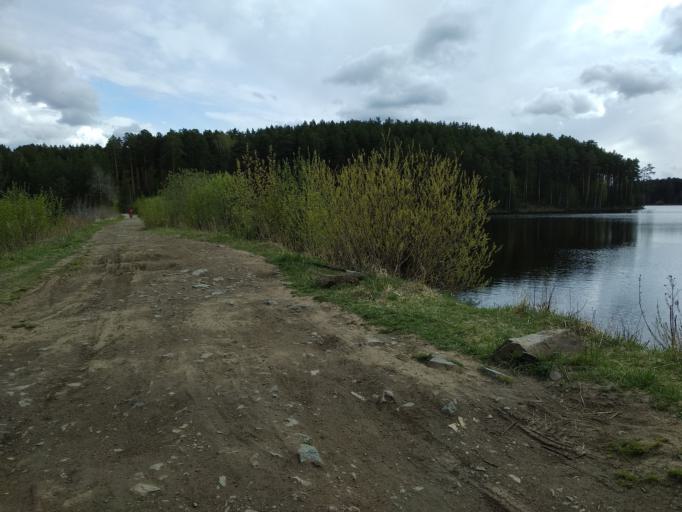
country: RU
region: Sverdlovsk
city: Staropyshminsk
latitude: 56.9211
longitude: 60.8558
